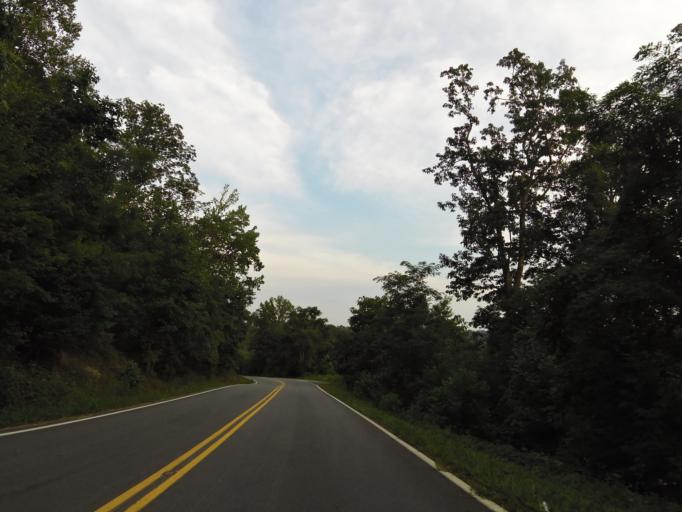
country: US
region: Tennessee
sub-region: Anderson County
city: Clinton
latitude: 36.1349
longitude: -84.2369
